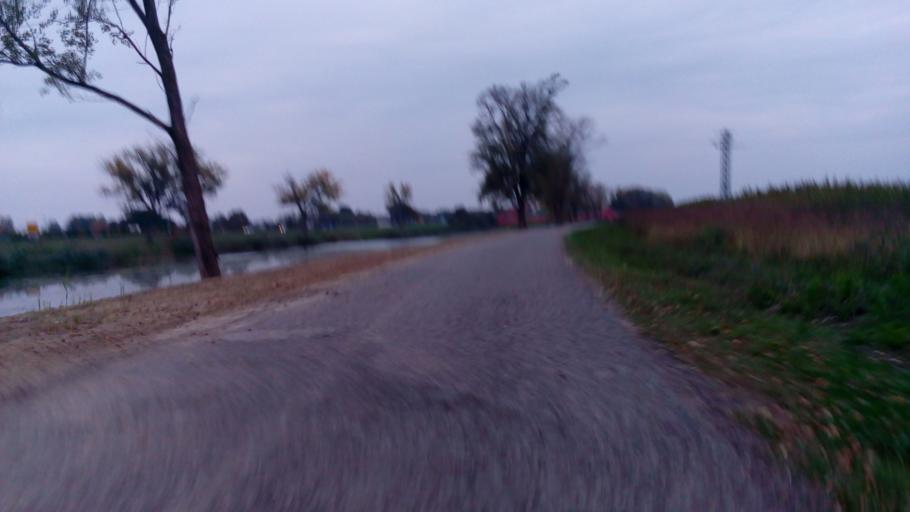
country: HR
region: Vukovarsko-Srijemska
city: Vinkovci
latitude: 45.2630
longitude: 18.8120
